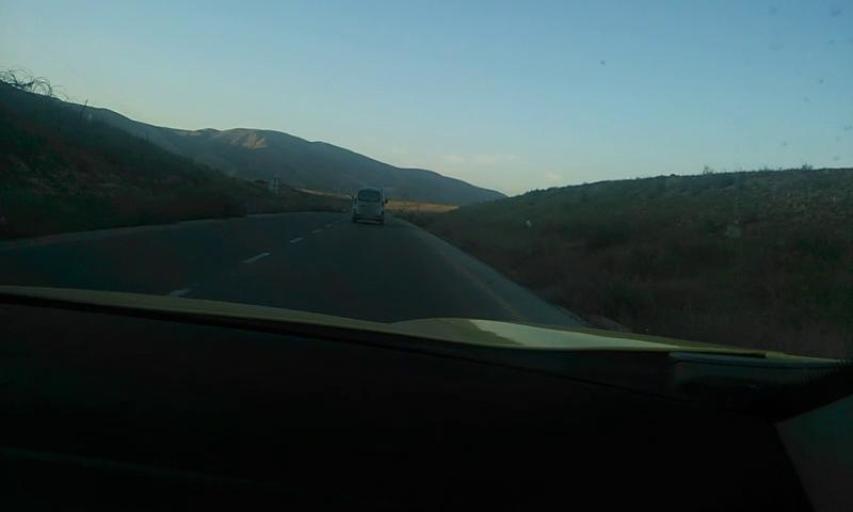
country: PS
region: West Bank
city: An Nuway`imah
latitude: 31.9131
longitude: 35.4216
